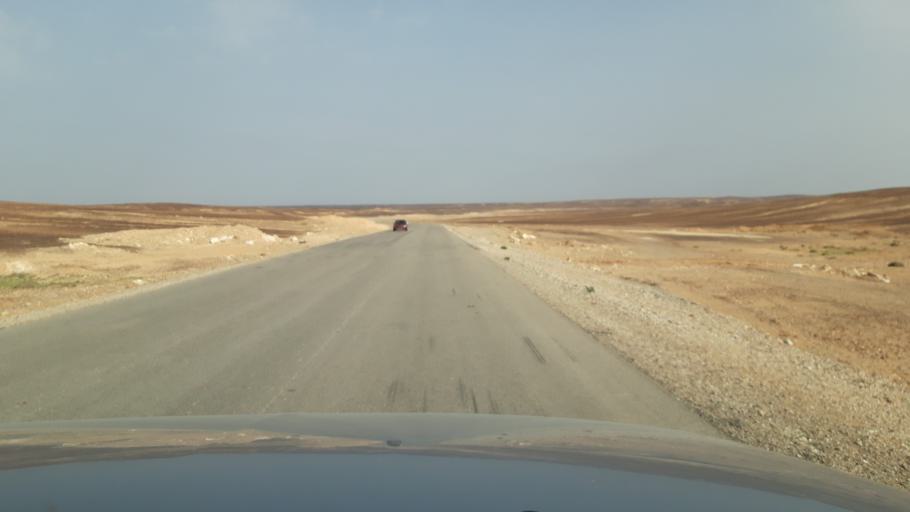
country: JO
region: Amman
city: Al Azraq ash Shamali
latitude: 31.2782
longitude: 36.5808
